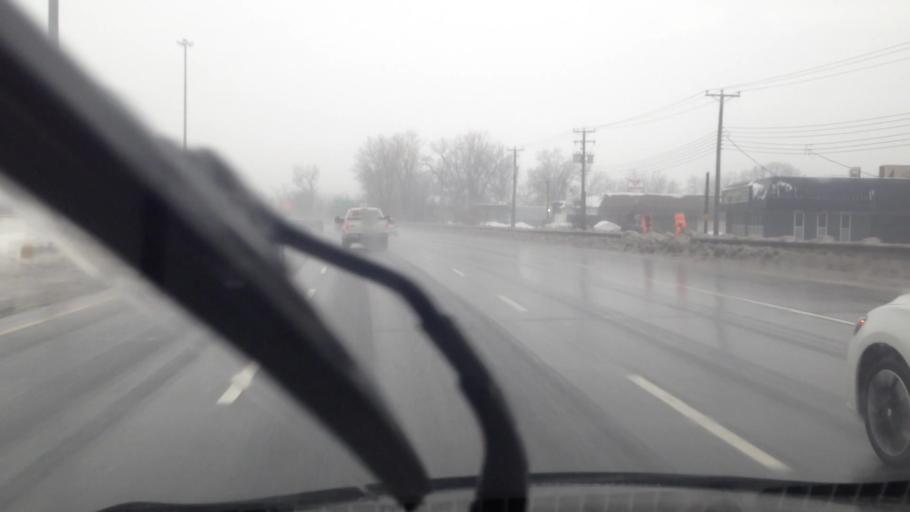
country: CA
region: Quebec
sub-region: Laurentides
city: Boisbriand
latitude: 45.6047
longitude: -73.8058
